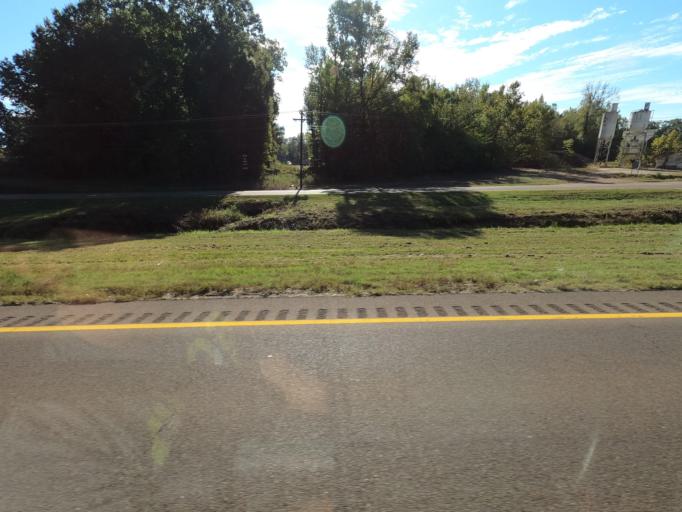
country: US
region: Tennessee
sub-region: Tipton County
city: Atoka
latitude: 35.4618
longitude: -89.7667
